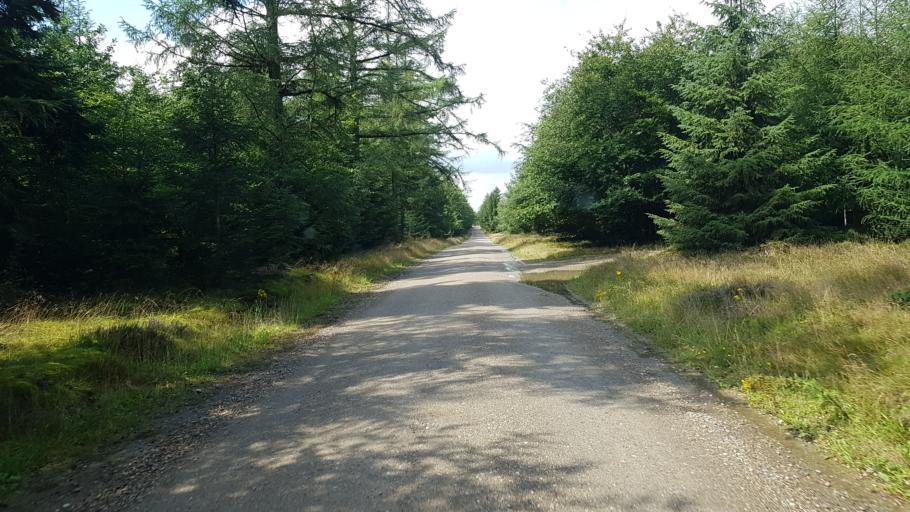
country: DK
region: South Denmark
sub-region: Vejen Kommune
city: Holsted
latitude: 55.5940
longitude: 8.9158
